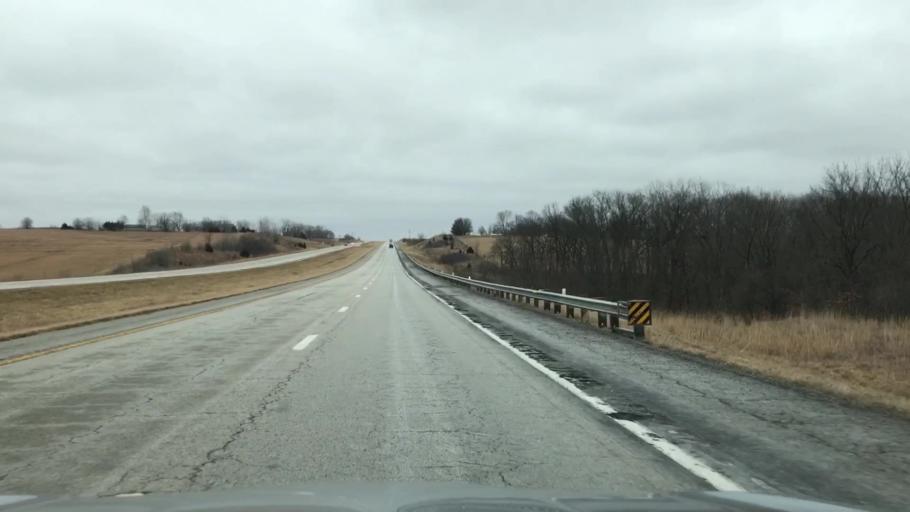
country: US
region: Missouri
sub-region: Caldwell County
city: Hamilton
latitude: 39.7499
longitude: -94.0993
